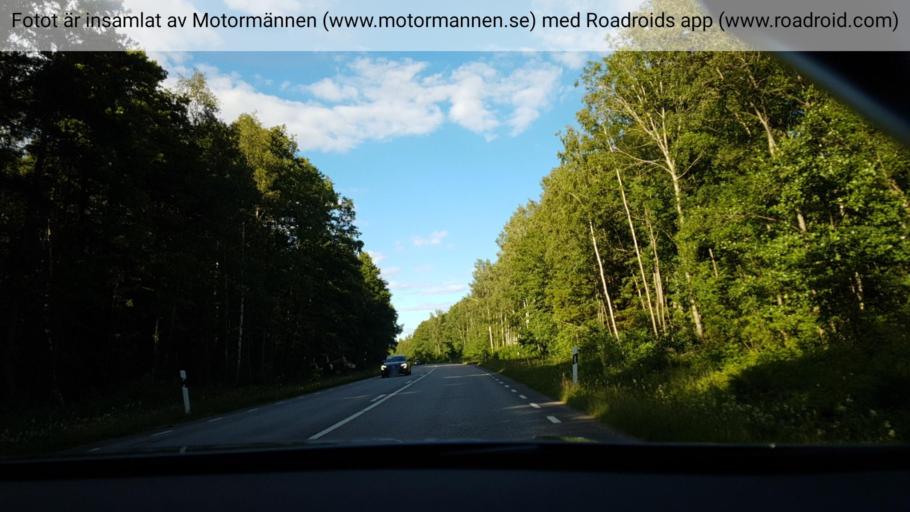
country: SE
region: Vaestra Goetaland
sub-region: Karlsborgs Kommun
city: Molltorp
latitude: 58.4795
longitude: 14.3468
